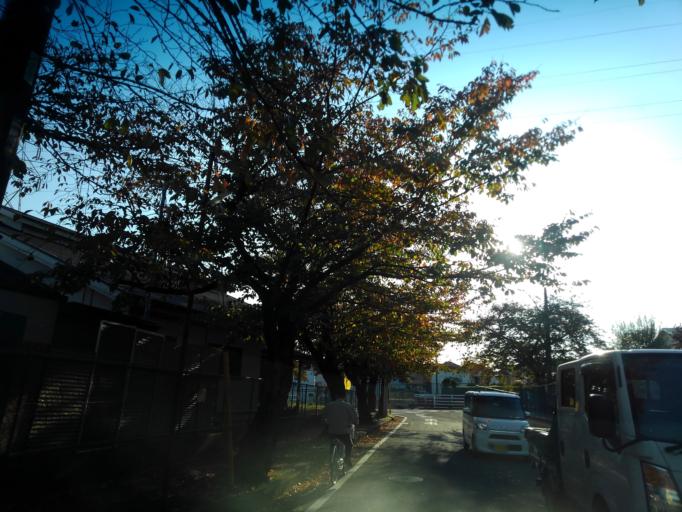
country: JP
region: Saitama
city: Tokorozawa
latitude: 35.7839
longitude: 139.4462
